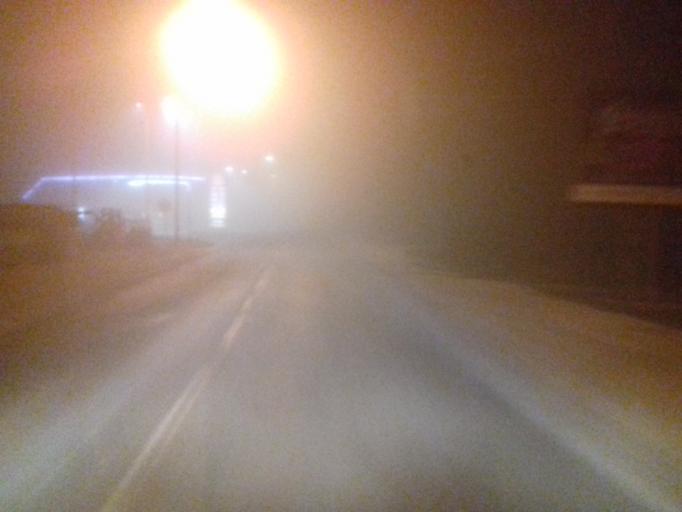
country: BA
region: Federation of Bosnia and Herzegovina
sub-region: Kanton Sarajevo
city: Sarajevo
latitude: 43.7798
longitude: 18.3603
